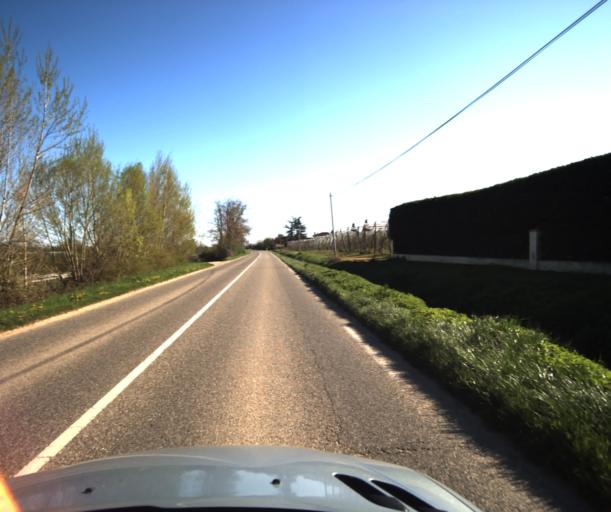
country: FR
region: Midi-Pyrenees
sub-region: Departement du Tarn-et-Garonne
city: Bressols
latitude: 43.9578
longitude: 1.3444
